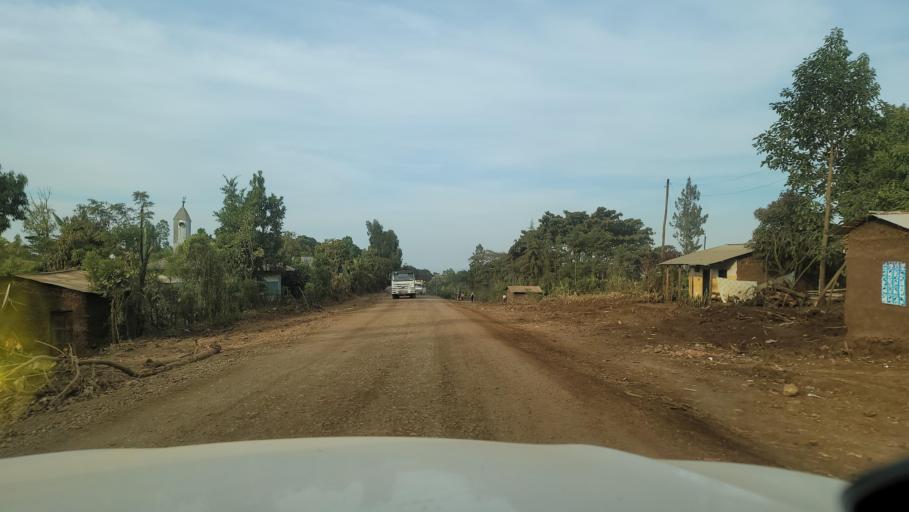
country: ET
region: Oromiya
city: Agaro
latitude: 7.8225
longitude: 36.5383
